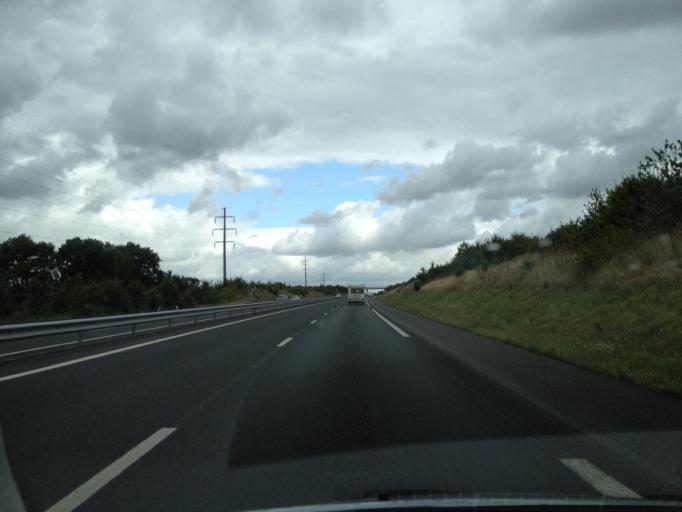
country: FR
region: Pays de la Loire
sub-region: Departement de Maine-et-Loire
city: Mazieres-en-Mauges
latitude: 47.0525
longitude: -0.8350
